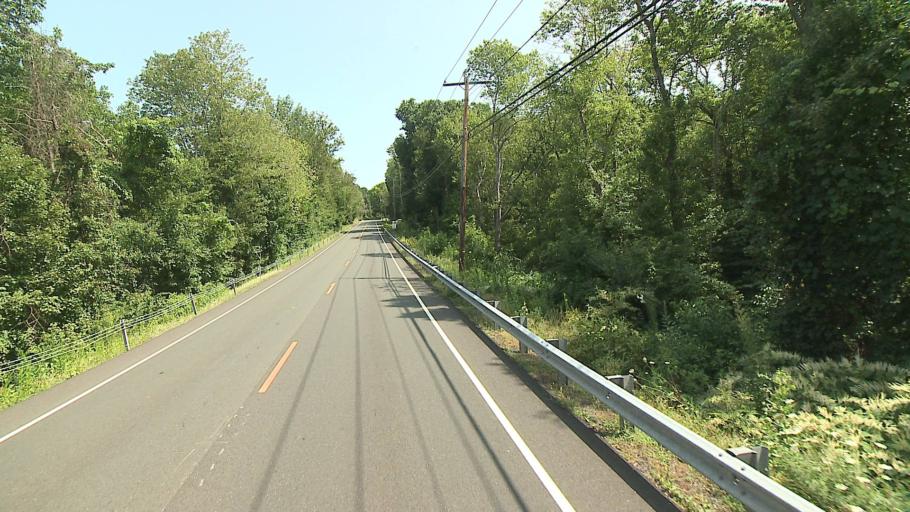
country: US
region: Connecticut
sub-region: Fairfield County
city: Shelton
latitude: 41.3343
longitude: -73.1575
